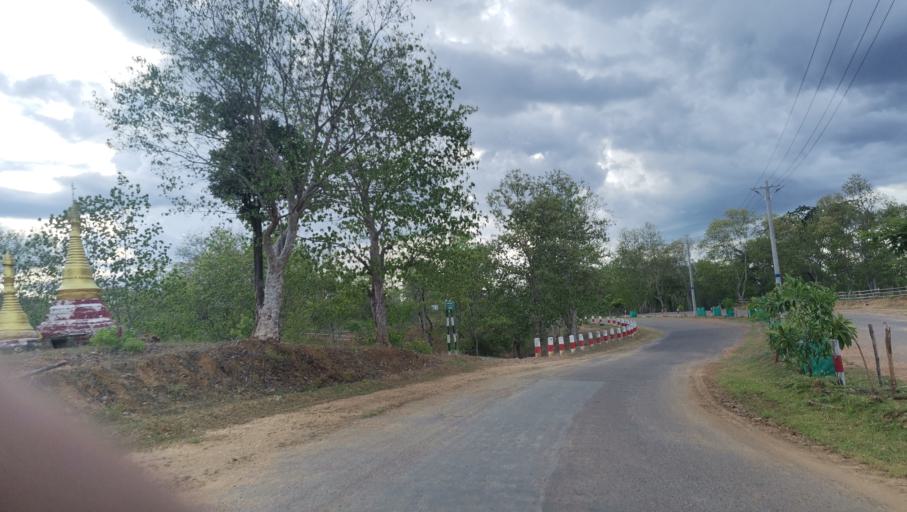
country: MM
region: Magway
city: Minbu
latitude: 20.0863
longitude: 94.5769
